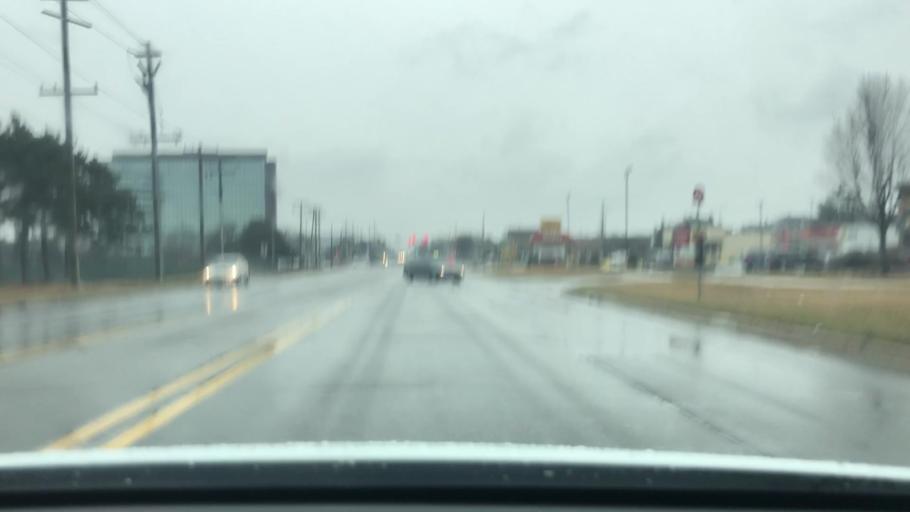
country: US
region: Michigan
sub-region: Oakland County
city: Clawson
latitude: 42.5637
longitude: -83.1675
